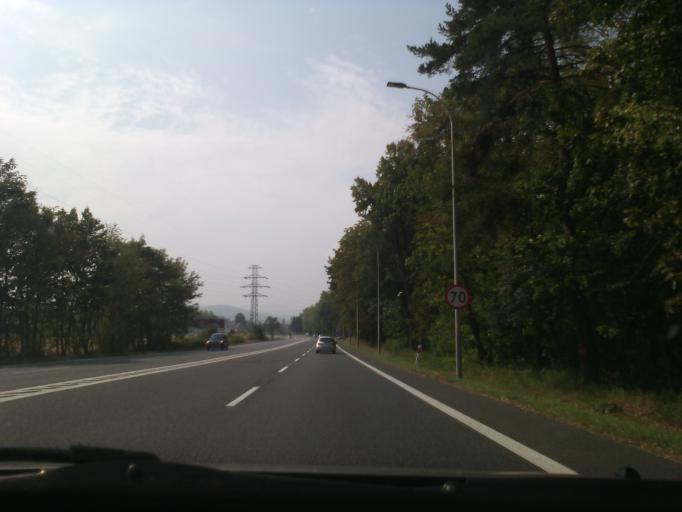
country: PL
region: Lower Silesian Voivodeship
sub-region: Powiat swidnicki
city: Swiebodzice
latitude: 50.8347
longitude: 16.3068
